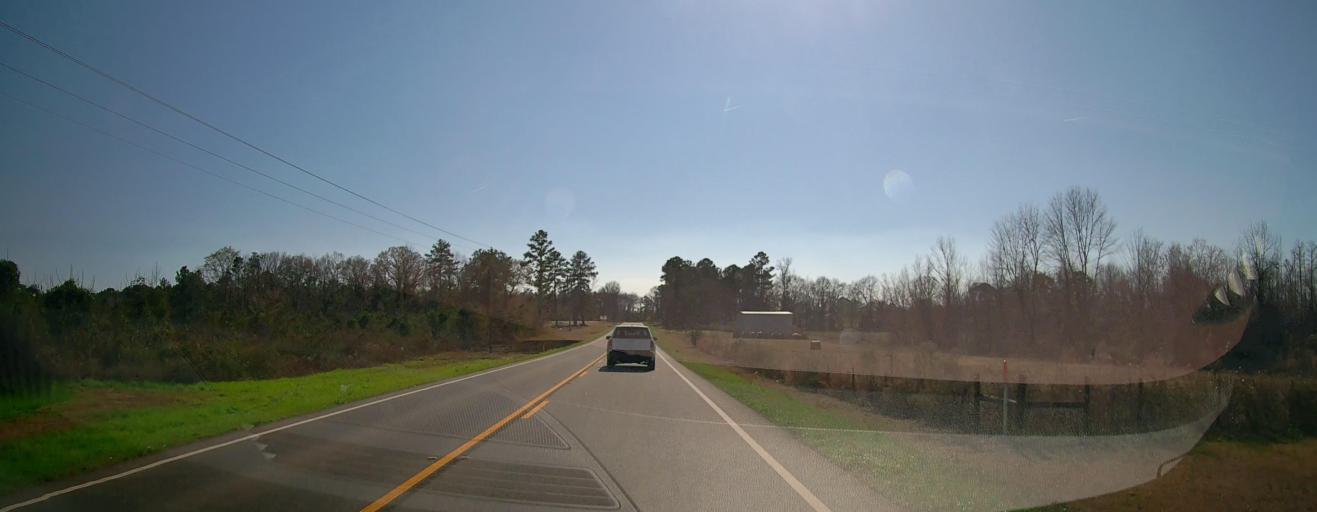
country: US
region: Georgia
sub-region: Macon County
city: Montezuma
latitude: 32.2966
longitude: -83.9133
